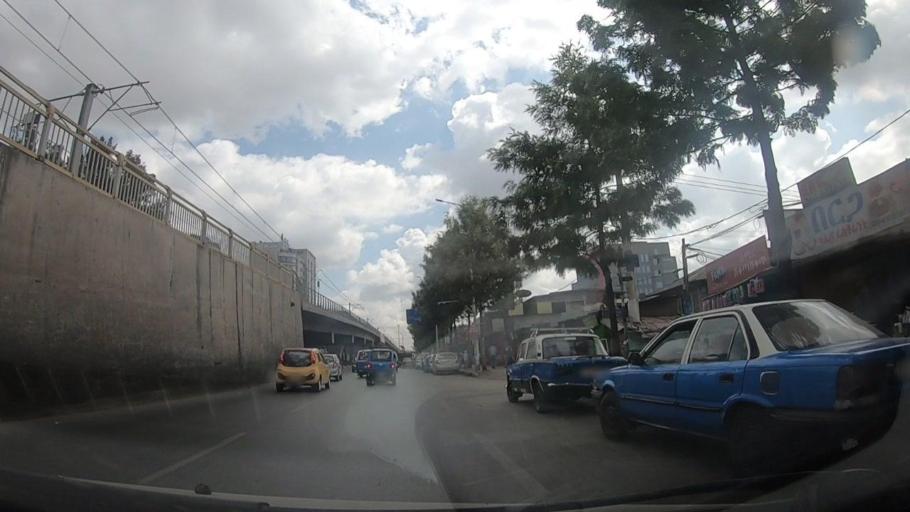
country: ET
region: Adis Abeba
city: Addis Ababa
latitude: 9.0116
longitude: 38.7328
